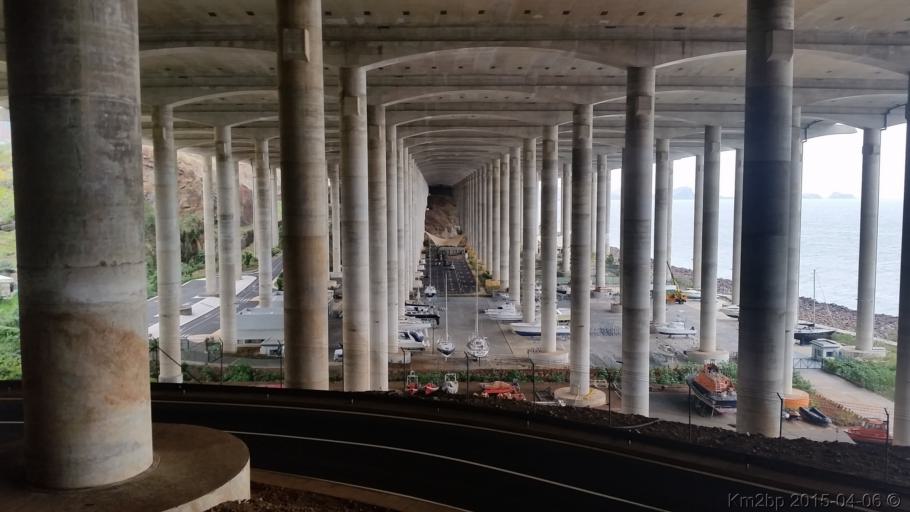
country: PT
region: Madeira
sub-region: Machico
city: Machico
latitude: 32.6987
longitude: -16.7710
